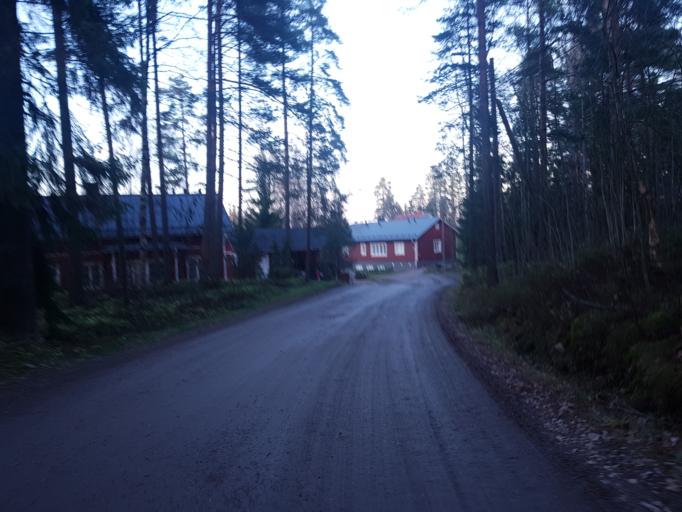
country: FI
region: Uusimaa
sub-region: Helsinki
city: Helsinki
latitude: 60.2790
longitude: 24.9280
